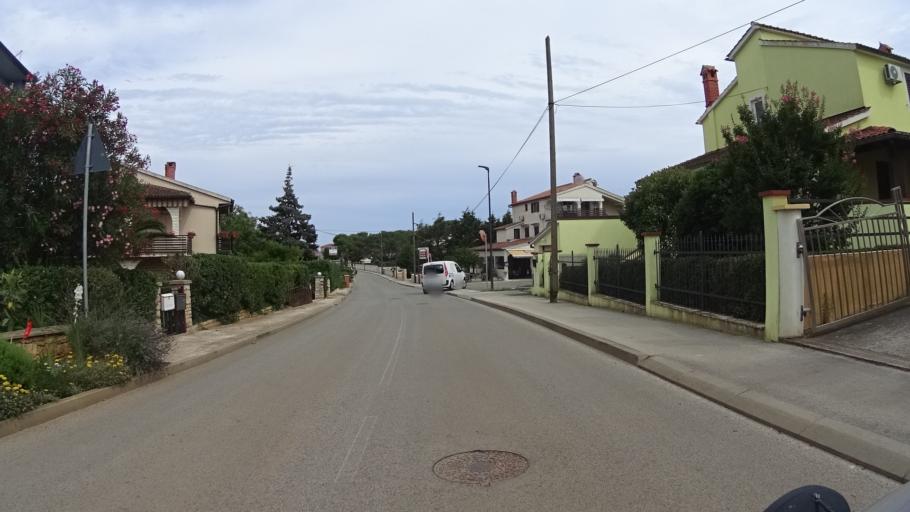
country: HR
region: Istarska
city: Medulin
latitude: 44.8251
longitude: 13.8930
